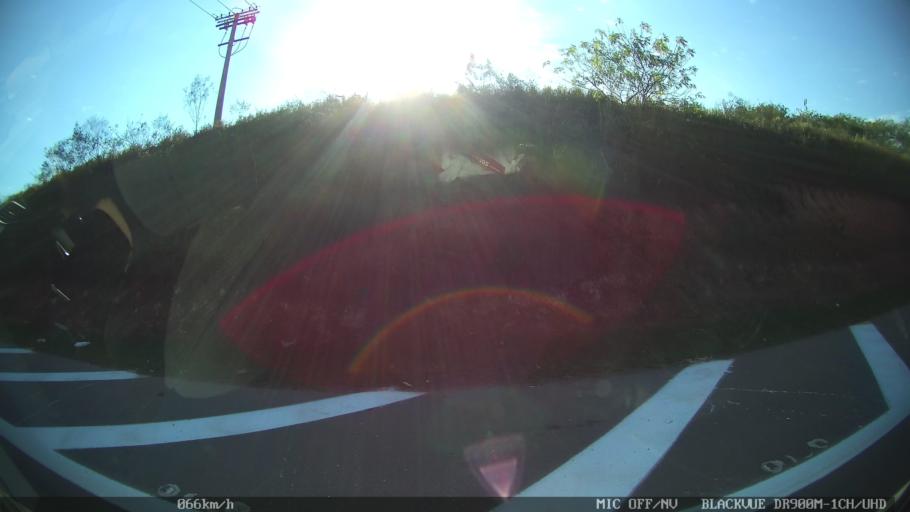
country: BR
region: Sao Paulo
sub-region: Piracicaba
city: Piracicaba
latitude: -22.6638
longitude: -47.6160
